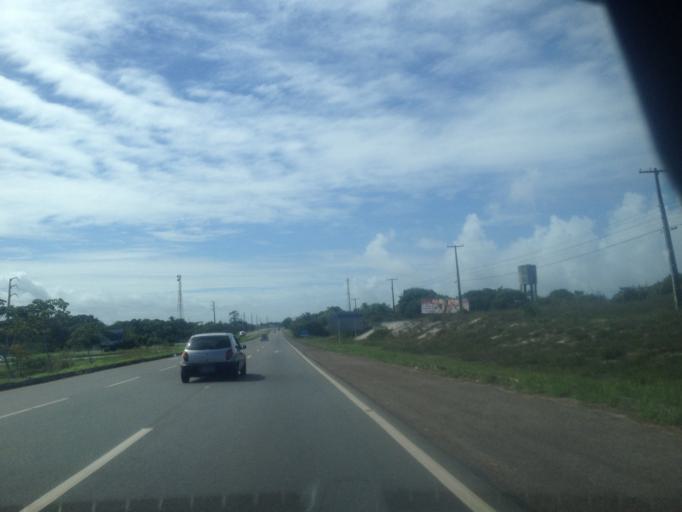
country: BR
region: Bahia
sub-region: Camacari
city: Camacari
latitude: -12.6563
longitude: -38.0874
